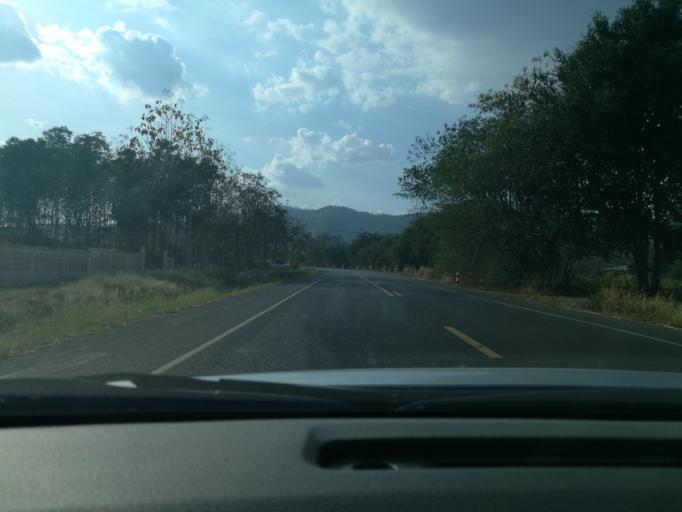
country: TH
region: Phetchabun
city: Phetchabun
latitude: 16.5484
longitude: 101.1276
